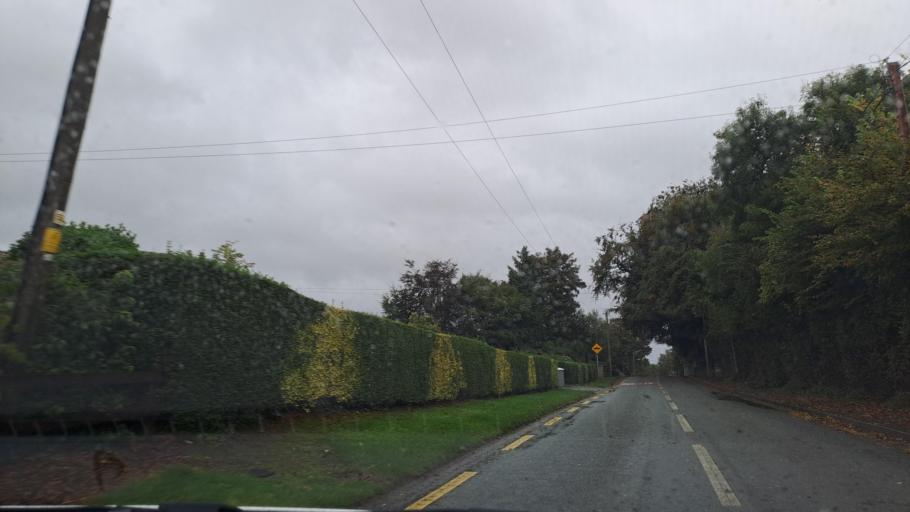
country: IE
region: Leinster
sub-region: Lu
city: Dundalk
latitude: 53.9689
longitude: -6.4803
